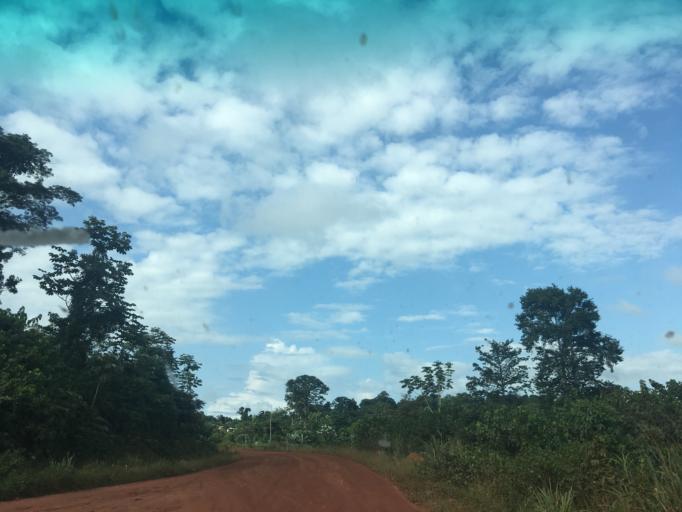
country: GH
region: Western
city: Wassa-Akropong
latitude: 5.9549
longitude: -2.4342
